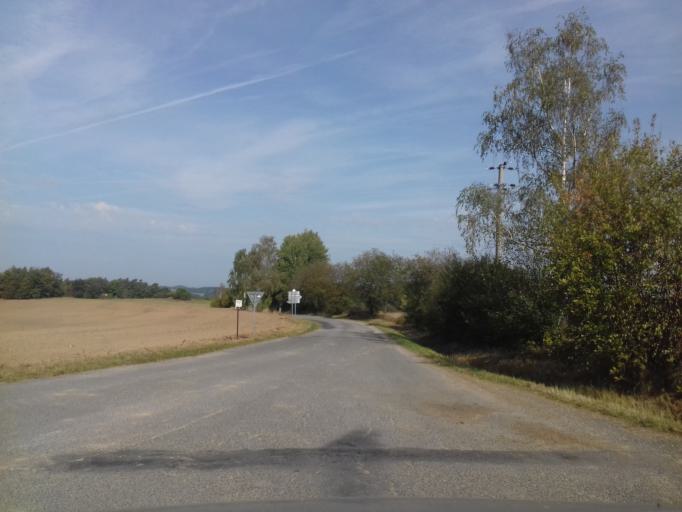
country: CZ
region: Central Bohemia
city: Kosova Hora
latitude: 49.6597
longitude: 14.5401
